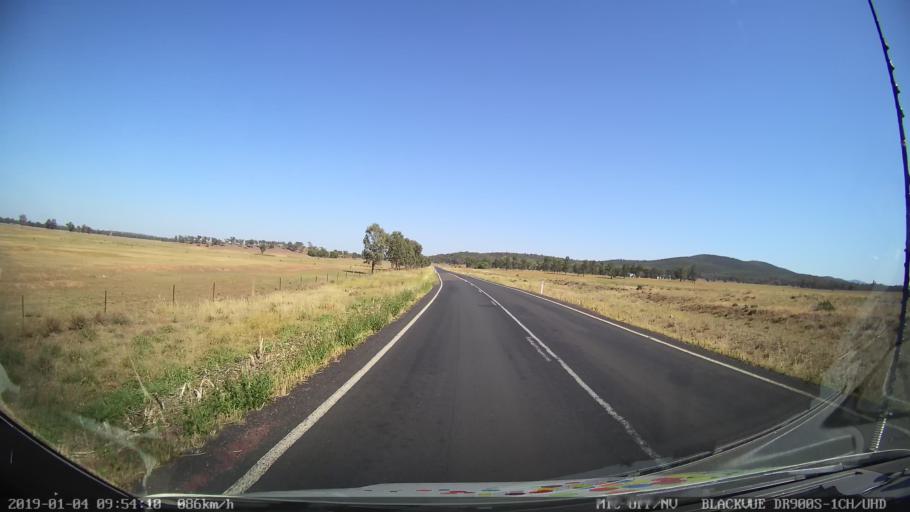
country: AU
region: New South Wales
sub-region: Cabonne
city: Canowindra
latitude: -33.5437
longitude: 148.4178
